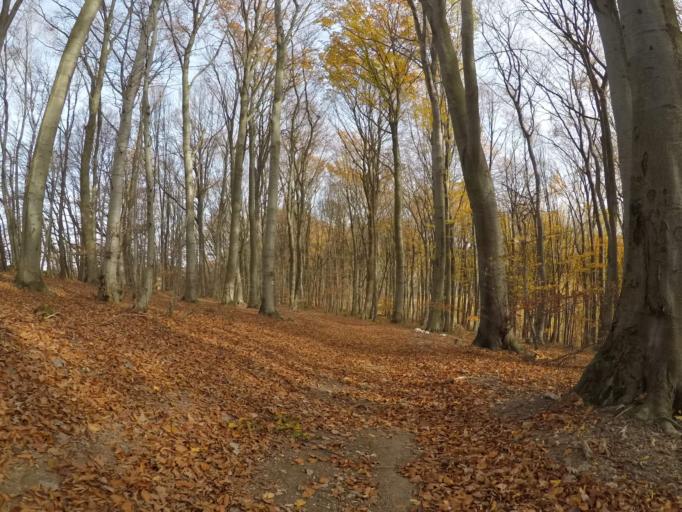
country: SK
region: Presovsky
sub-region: Okres Presov
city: Presov
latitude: 48.9165
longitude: 21.2183
